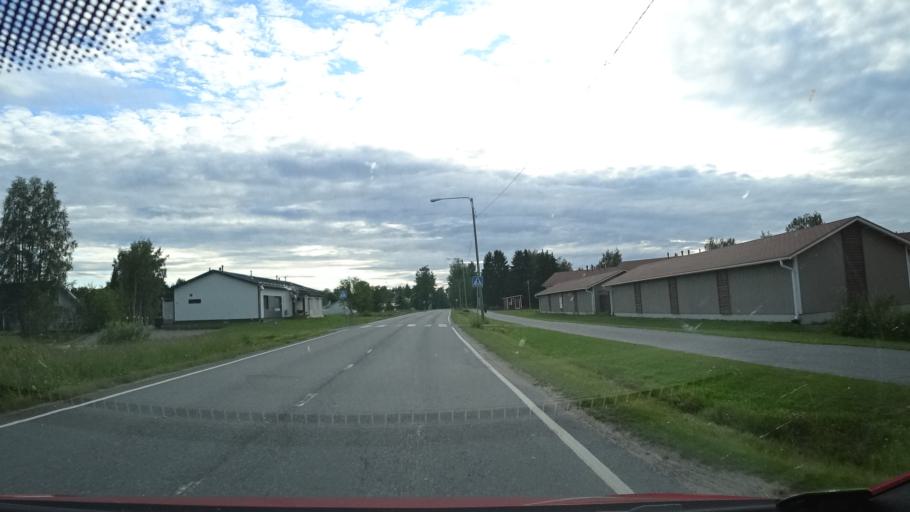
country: FI
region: Northern Ostrobothnia
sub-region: Oulu
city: Liminka
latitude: 64.8080
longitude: 25.4289
